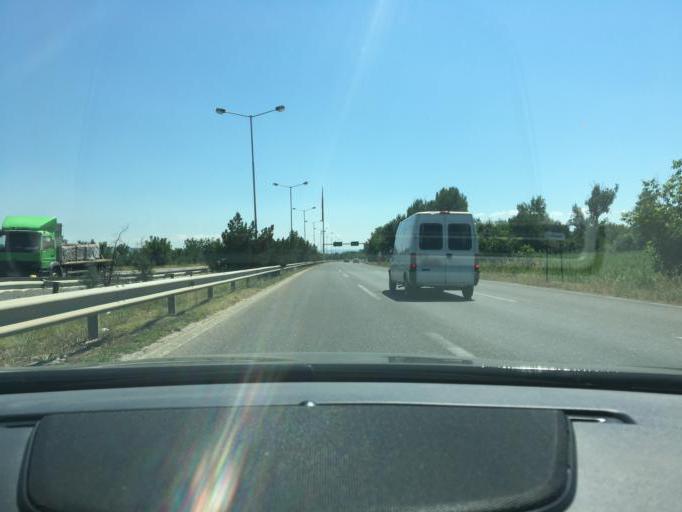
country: MK
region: Ilinden
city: Jurumleri
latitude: 41.9971
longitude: 21.5194
